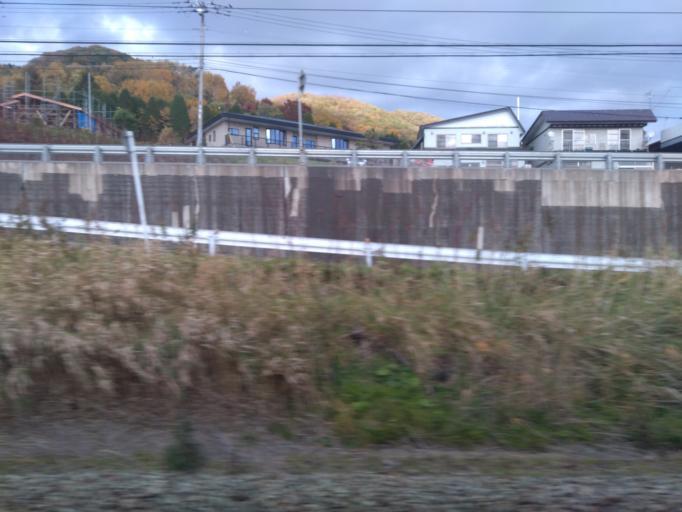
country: JP
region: Hokkaido
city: Niseko Town
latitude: 42.5865
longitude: 140.7090
